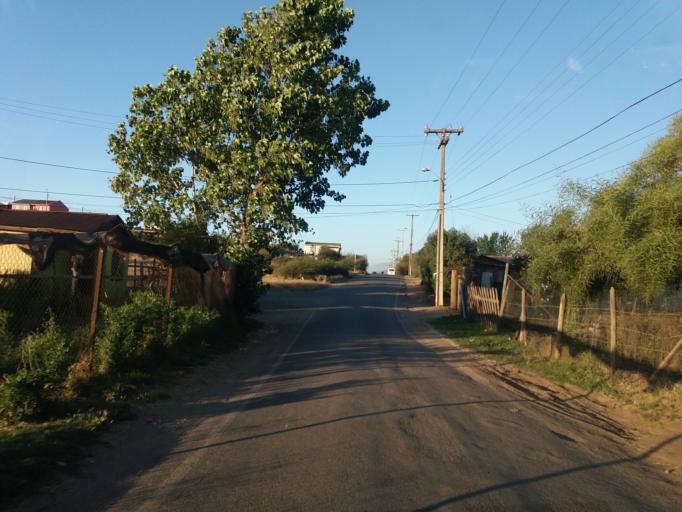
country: CL
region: Valparaiso
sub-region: Provincia de Quillota
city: Quillota
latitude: -32.9456
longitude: -71.2717
